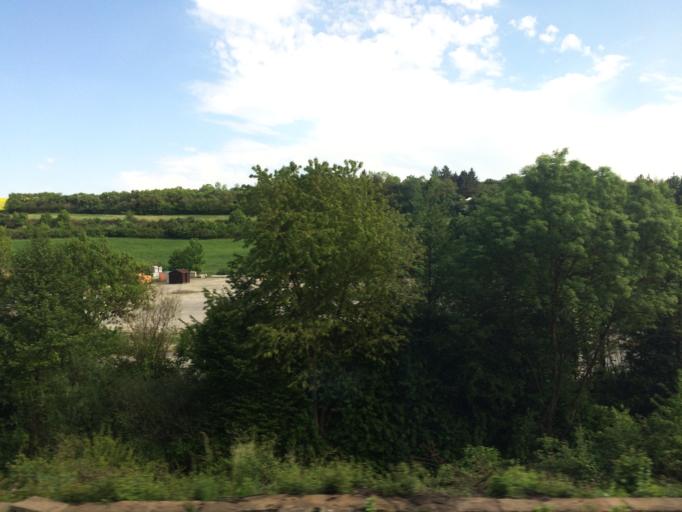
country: DE
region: Bavaria
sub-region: Regierungsbezirk Unterfranken
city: Rottendorf
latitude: 49.7990
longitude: 10.0321
